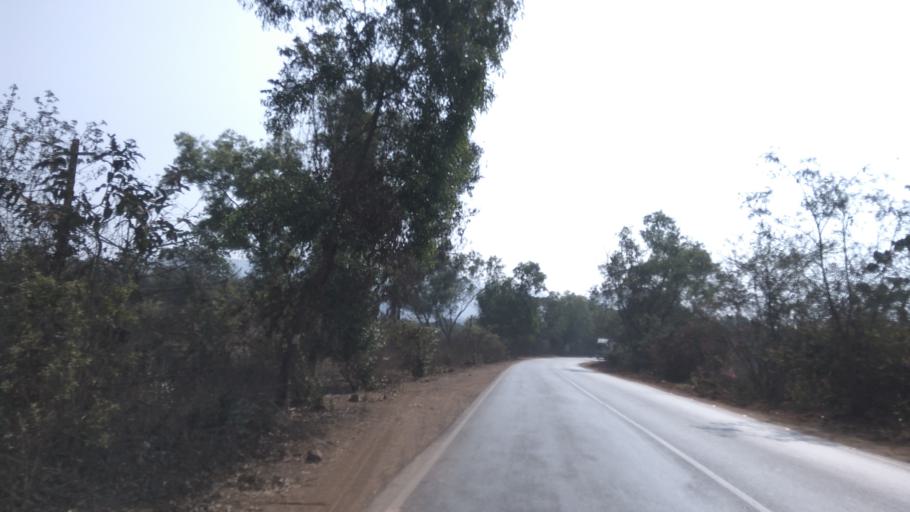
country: IN
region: Goa
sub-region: North Goa
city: Palle
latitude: 15.4150
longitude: 74.0774
